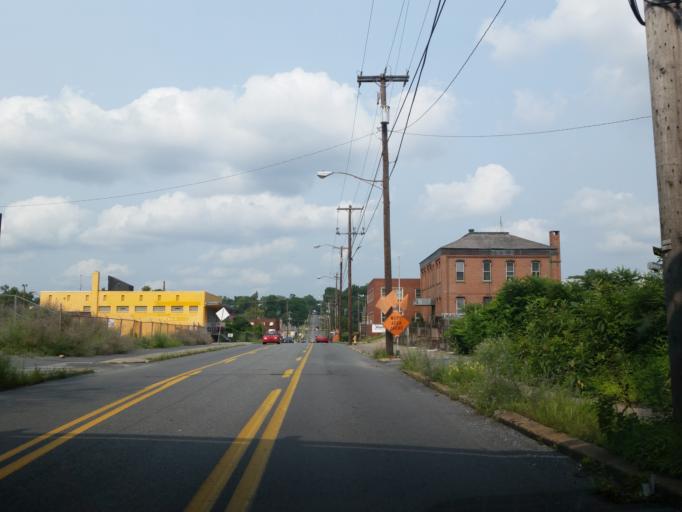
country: US
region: Pennsylvania
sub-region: Dauphin County
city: Harrisburg
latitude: 40.2710
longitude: -76.8806
